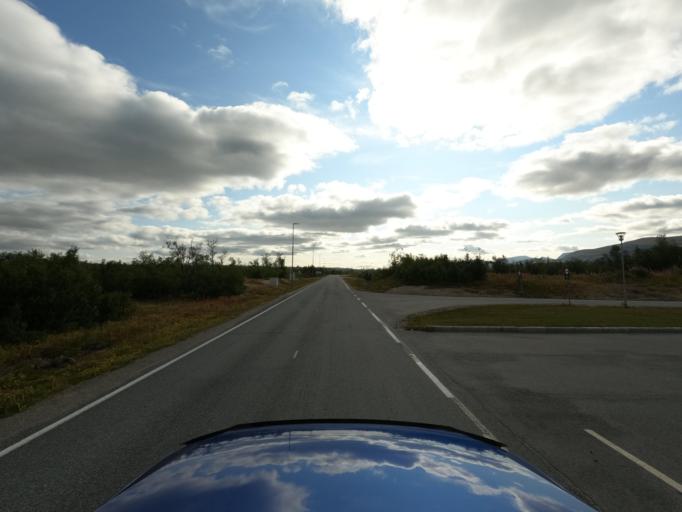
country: NO
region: Finnmark Fylke
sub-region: Porsanger
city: Lakselv
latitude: 70.0655
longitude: 24.9847
